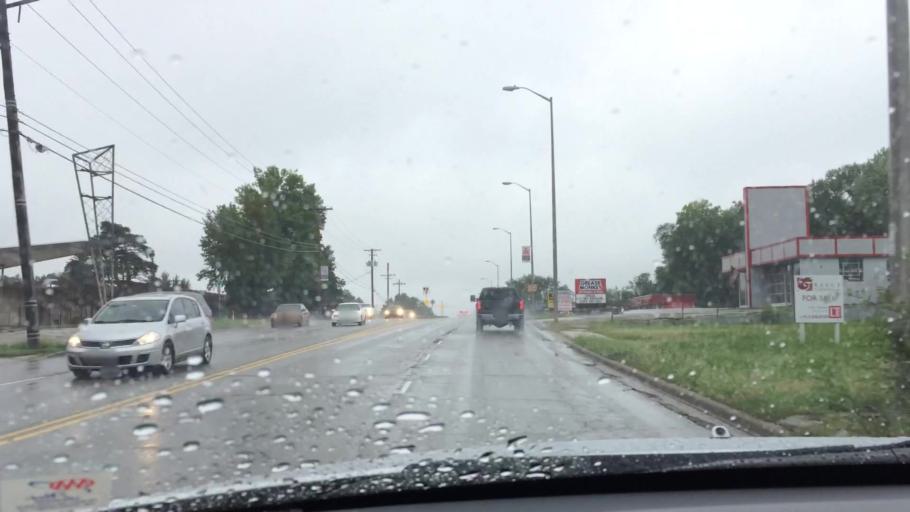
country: US
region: Kansas
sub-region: Johnson County
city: Overland Park
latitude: 38.9810
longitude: -94.6677
